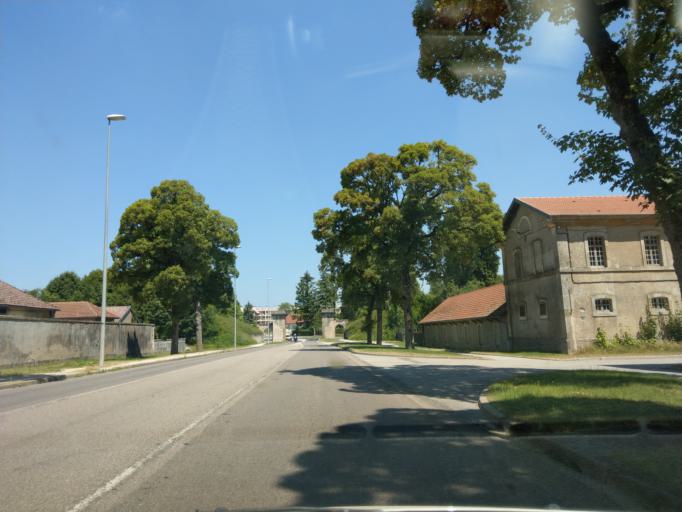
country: FR
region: Champagne-Ardenne
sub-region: Departement de la Haute-Marne
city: Langres
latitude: 47.8511
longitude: 5.3339
